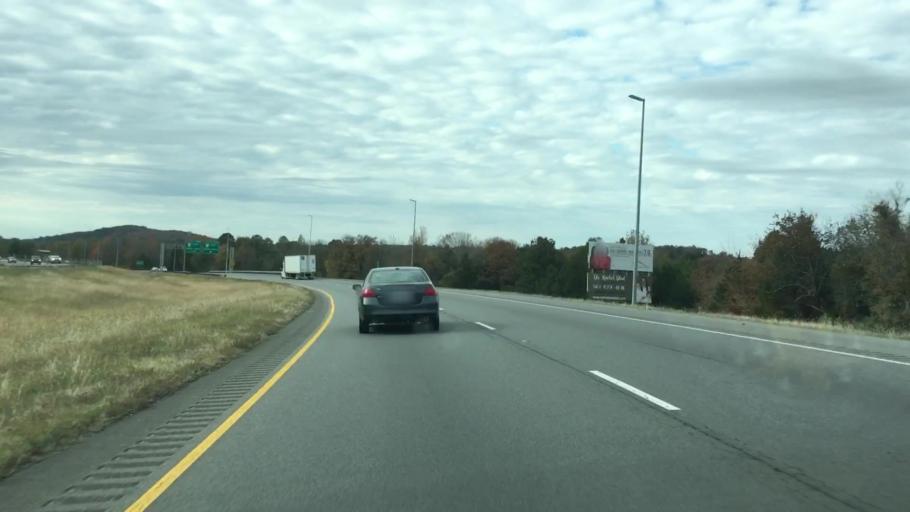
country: US
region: Arkansas
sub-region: Faulkner County
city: Conway
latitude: 35.1181
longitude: -92.4512
